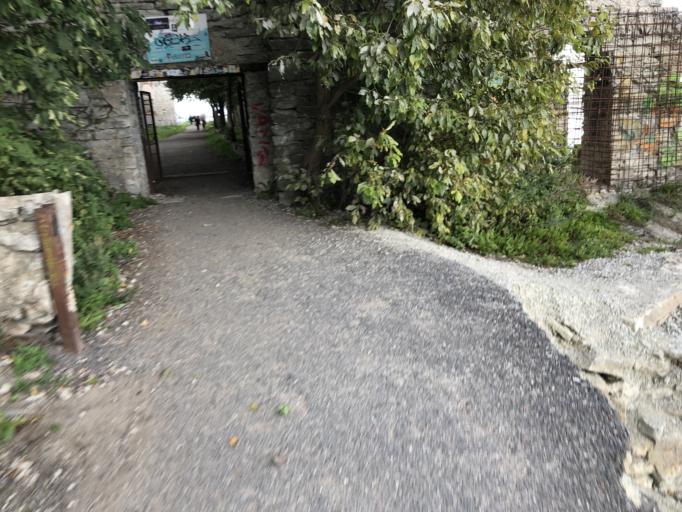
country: EE
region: Harju
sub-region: Tallinna linn
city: Tallinn
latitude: 59.4495
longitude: 24.7438
